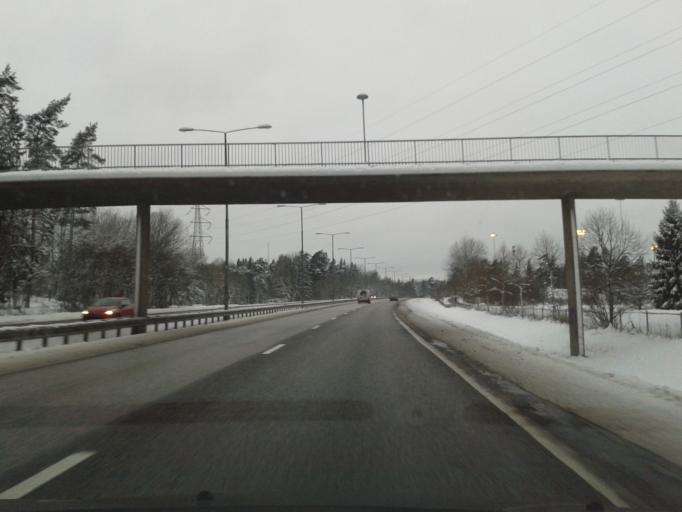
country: SE
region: Stockholm
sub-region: Stockholms Kommun
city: Arsta
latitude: 59.2595
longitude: 18.0730
